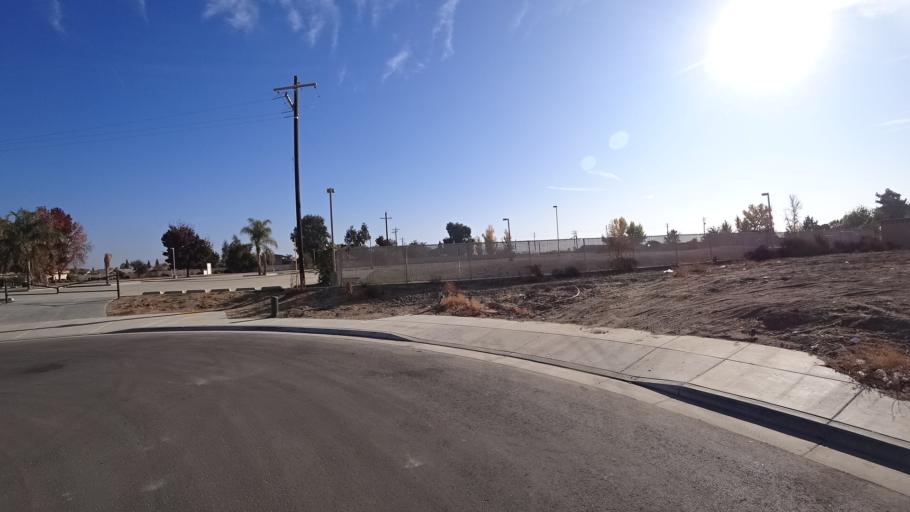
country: US
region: California
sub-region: Kern County
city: Greenfield
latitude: 35.2676
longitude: -119.0636
